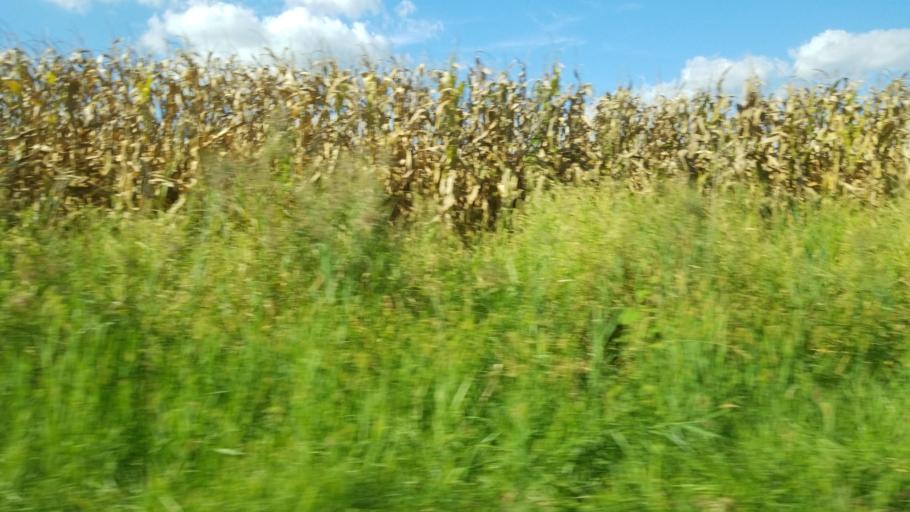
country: US
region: Illinois
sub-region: Saline County
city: Harrisburg
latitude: 37.8272
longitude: -88.5453
